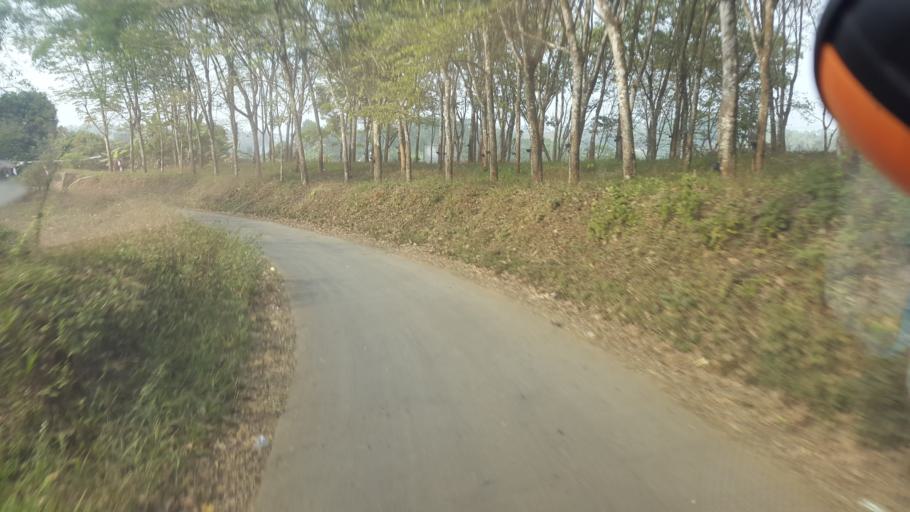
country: ID
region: West Java
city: Cilandak
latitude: -6.9385
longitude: 106.7387
